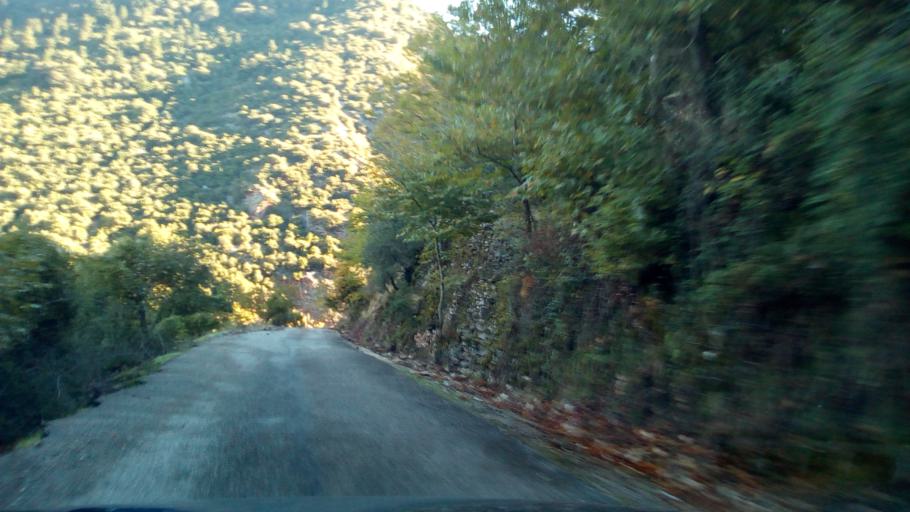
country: GR
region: West Greece
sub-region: Nomos Aitolias kai Akarnanias
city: Nafpaktos
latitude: 38.5538
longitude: 21.8550
